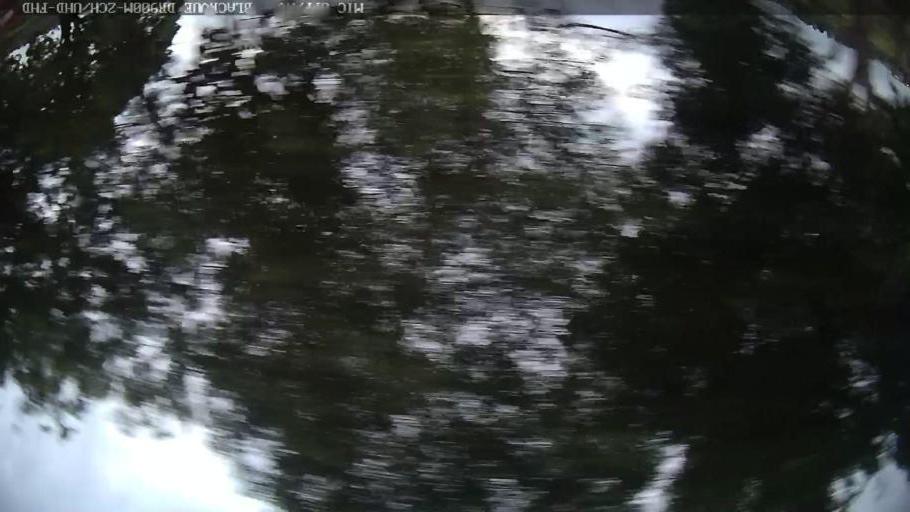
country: BR
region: Sao Paulo
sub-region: Itupeva
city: Itupeva
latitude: -23.1426
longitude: -47.0080
